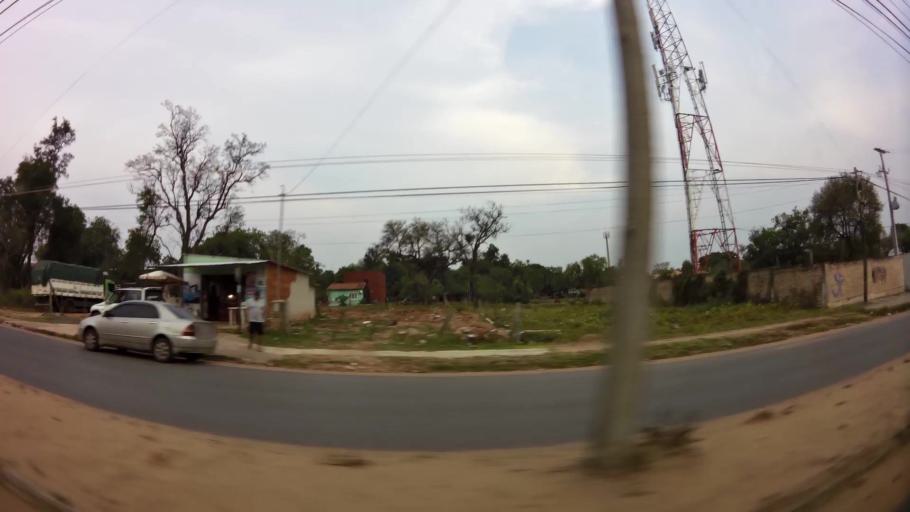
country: PY
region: Central
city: Lambare
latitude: -25.3551
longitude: -57.6431
